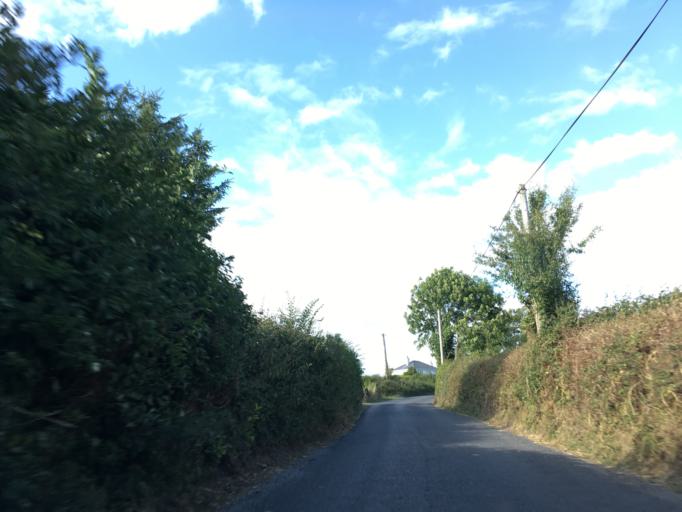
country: IE
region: Munster
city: Cahir
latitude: 52.2876
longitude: -7.9550
